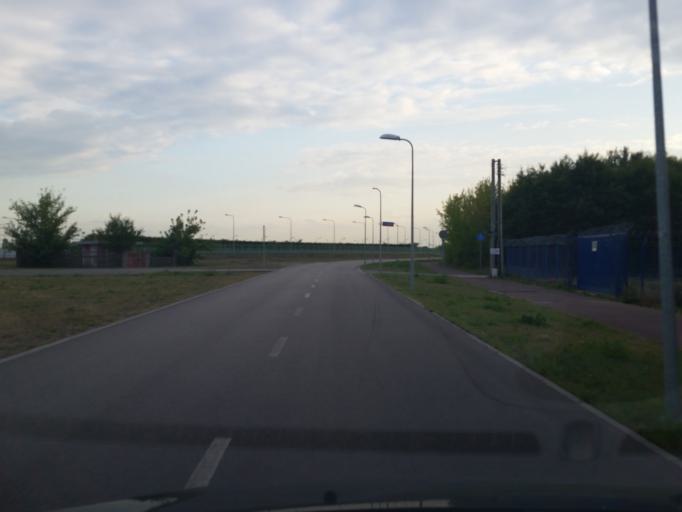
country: PL
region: Masovian Voivodeship
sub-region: Powiat piaseczynski
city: Mysiadlo
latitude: 52.1424
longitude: 20.9881
